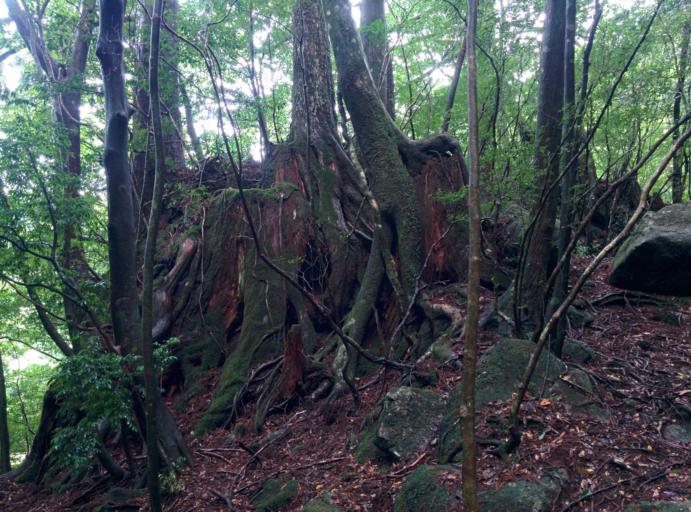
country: JP
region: Kagoshima
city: Nishinoomote
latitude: 30.3544
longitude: 130.5627
